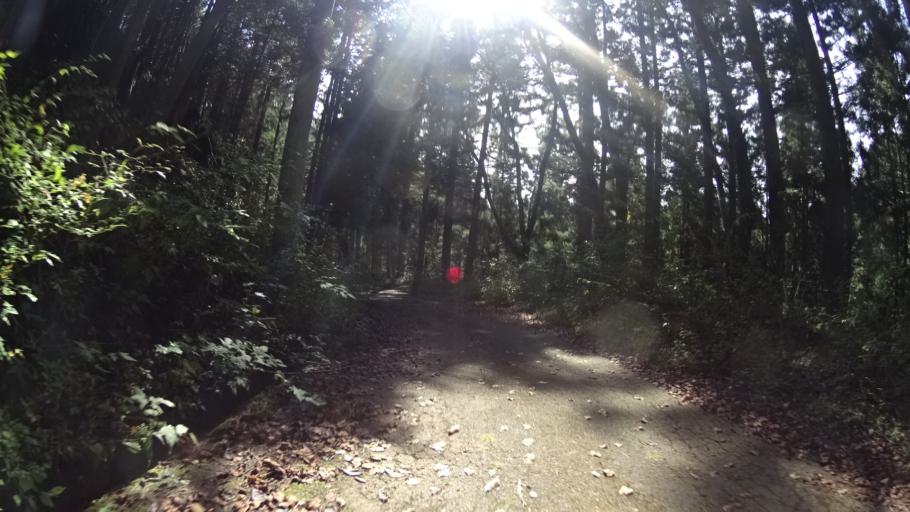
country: JP
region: Yamanashi
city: Otsuki
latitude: 35.5760
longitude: 138.9876
